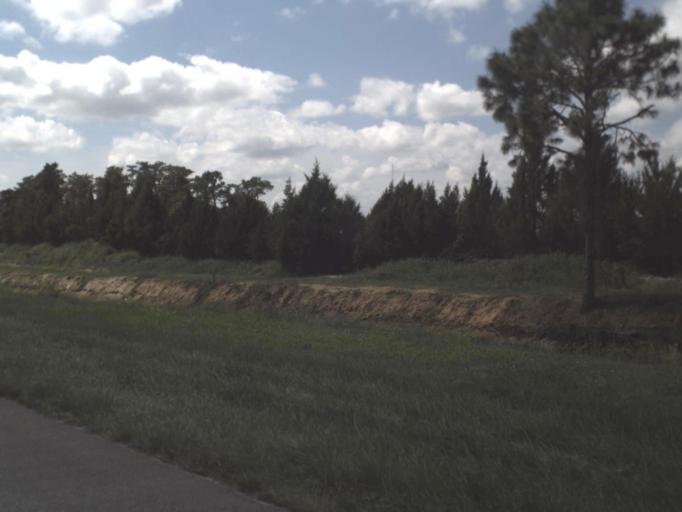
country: US
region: Florida
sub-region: Hendry County
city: LaBelle
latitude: 26.6952
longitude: -81.4370
